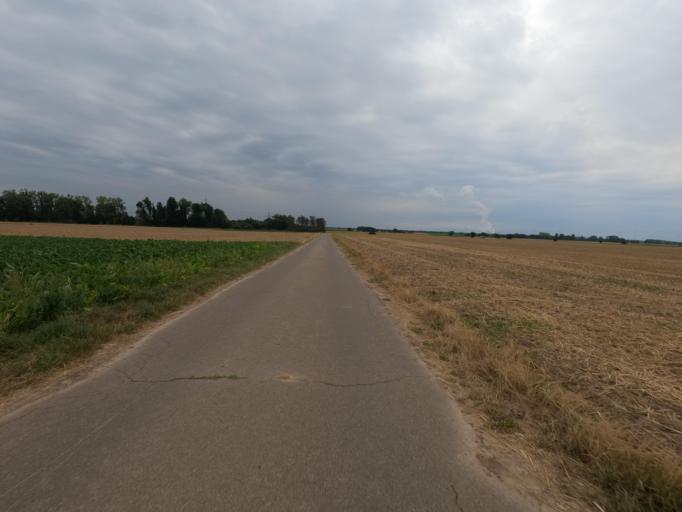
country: DE
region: North Rhine-Westphalia
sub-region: Regierungsbezirk Koln
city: Aldenhoven
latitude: 50.9317
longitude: 6.2998
